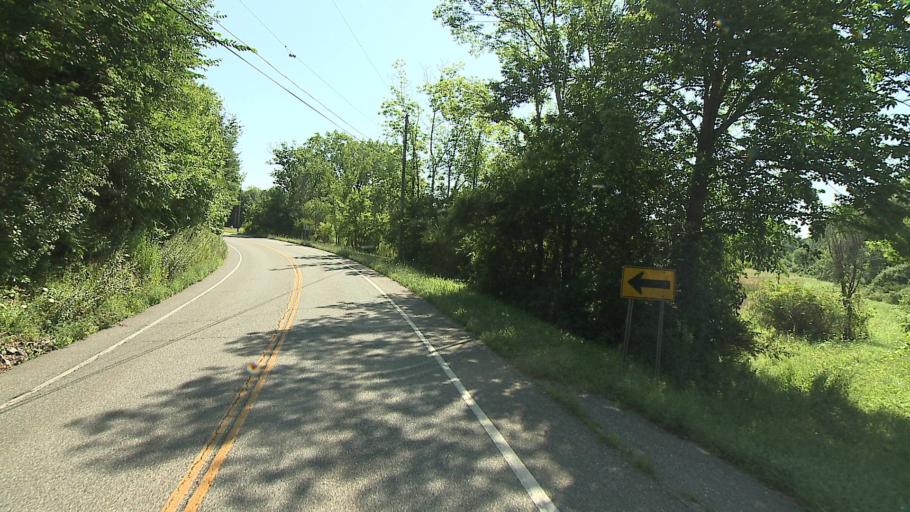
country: US
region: Connecticut
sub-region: Litchfield County
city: Kent
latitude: 41.8741
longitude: -73.4875
